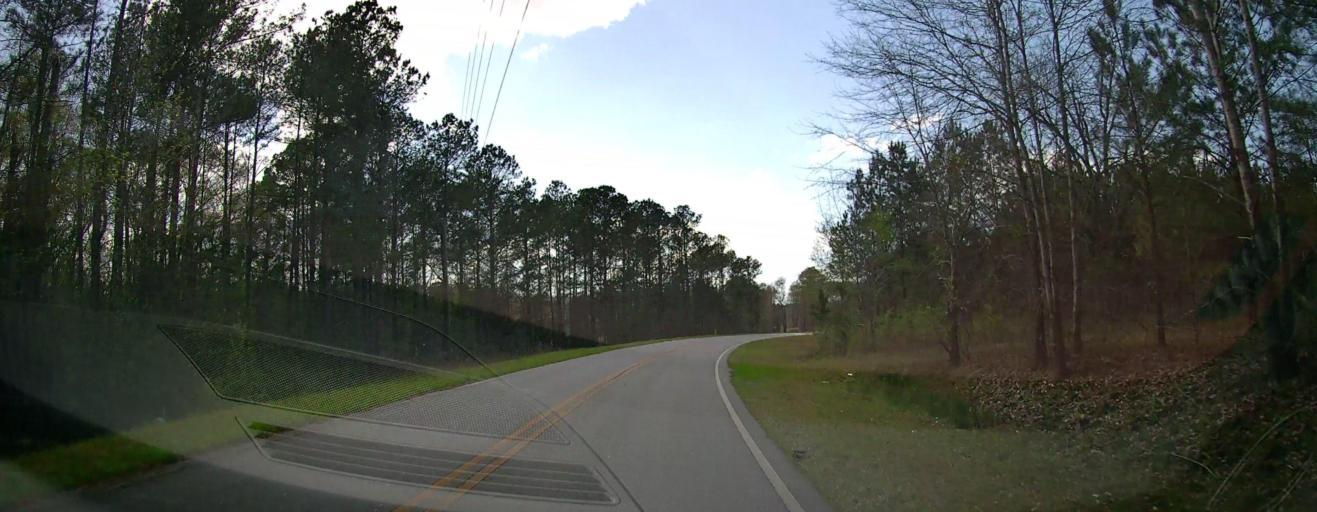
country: US
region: Georgia
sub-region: Wilkinson County
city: Gordon
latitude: 32.8258
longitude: -83.4211
